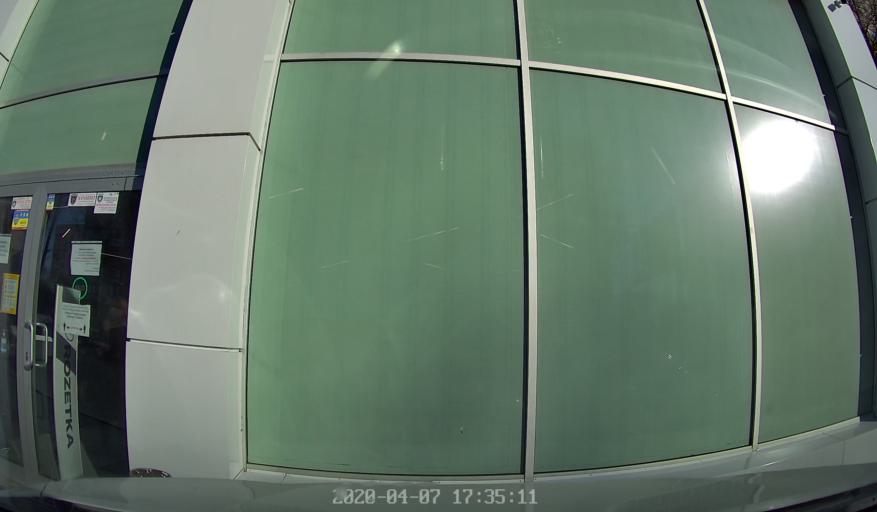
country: NG
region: Niger
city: Lemu
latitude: 9.2867
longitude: 6.1415
